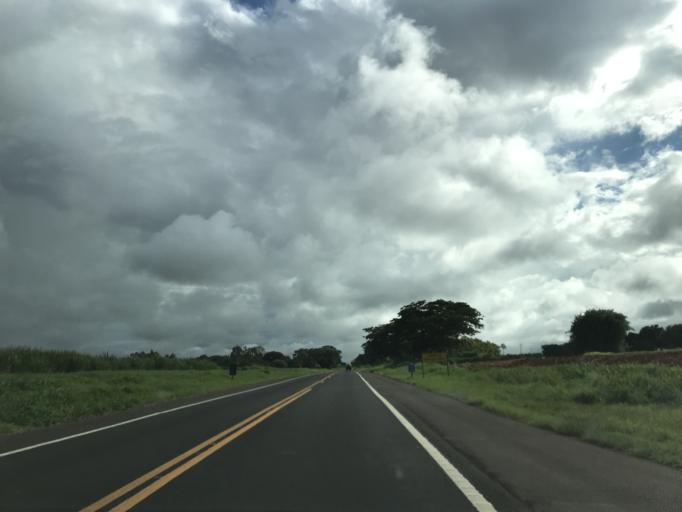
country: BR
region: Sao Paulo
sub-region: Penapolis
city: Penapolis
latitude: -21.4821
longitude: -50.2052
